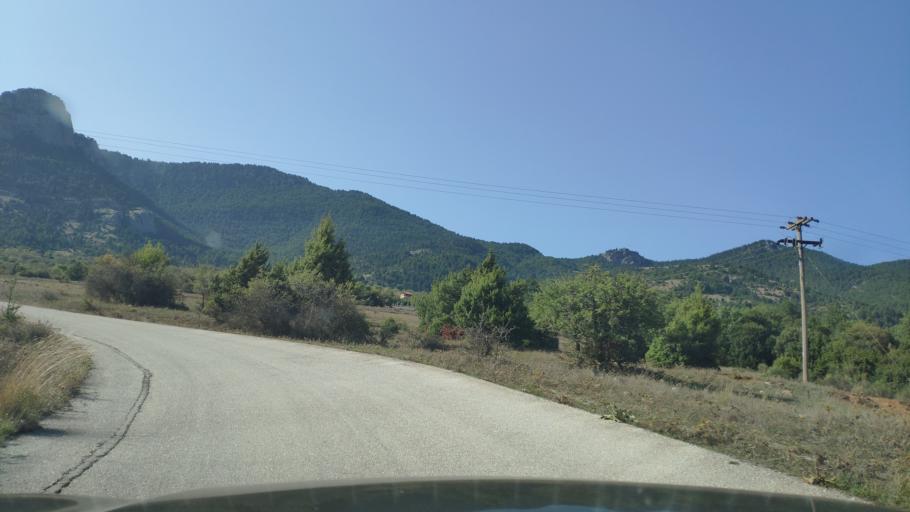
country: GR
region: West Greece
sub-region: Nomos Achaias
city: Aiyira
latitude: 37.9880
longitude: 22.3591
